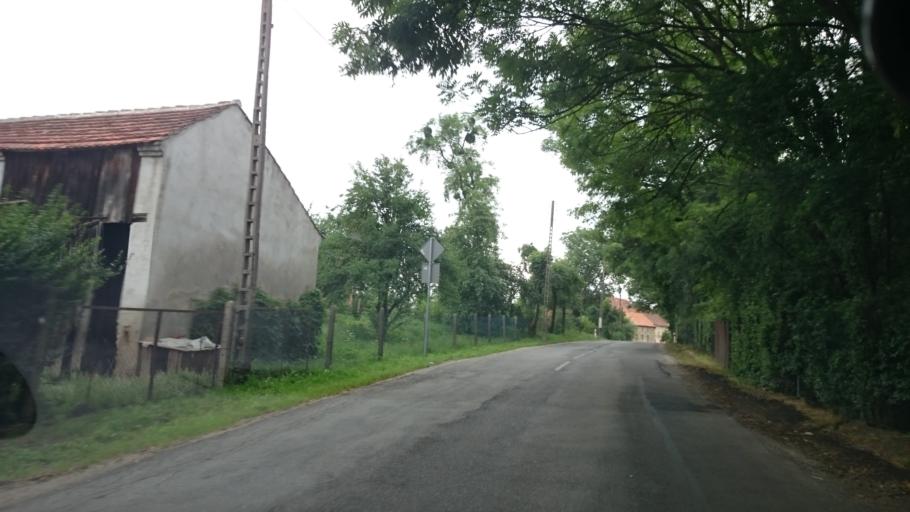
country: PL
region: Lower Silesian Voivodeship
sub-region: Powiat strzelinski
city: Przeworno
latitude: 50.6429
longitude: 17.2263
